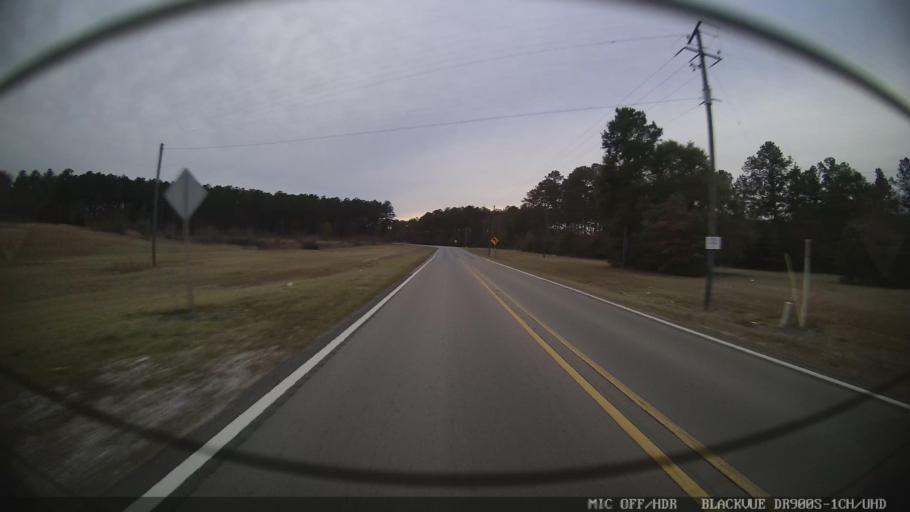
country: US
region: Mississippi
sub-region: Clarke County
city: Quitman
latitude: 32.0427
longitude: -88.7472
